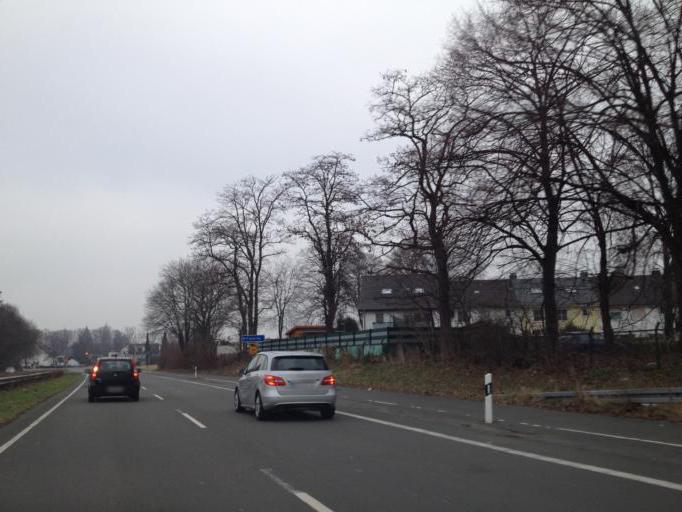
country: DE
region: North Rhine-Westphalia
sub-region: Regierungsbezirk Arnsberg
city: Soest
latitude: 51.5597
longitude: 8.1051
